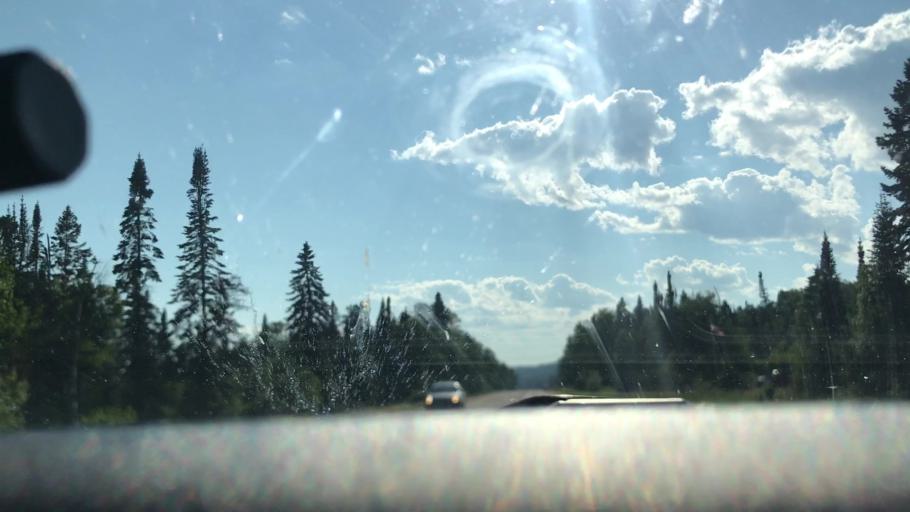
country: US
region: Minnesota
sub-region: Cook County
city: Grand Marais
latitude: 47.7958
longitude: -90.1356
